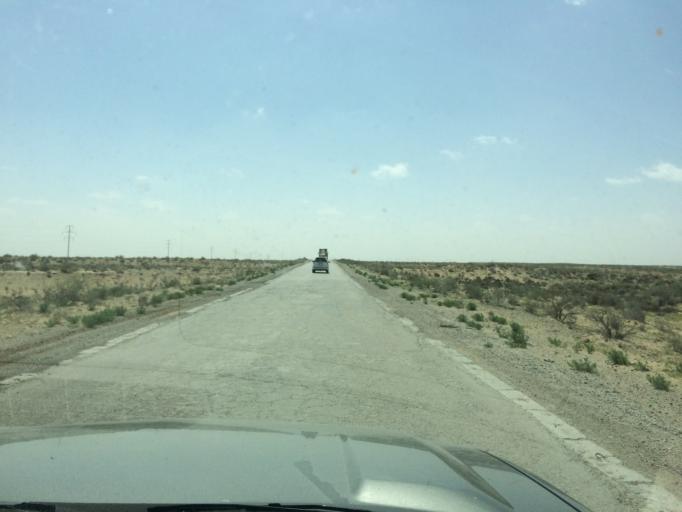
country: TM
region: Balkan
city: Gumdag
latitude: 38.8052
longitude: 54.5982
